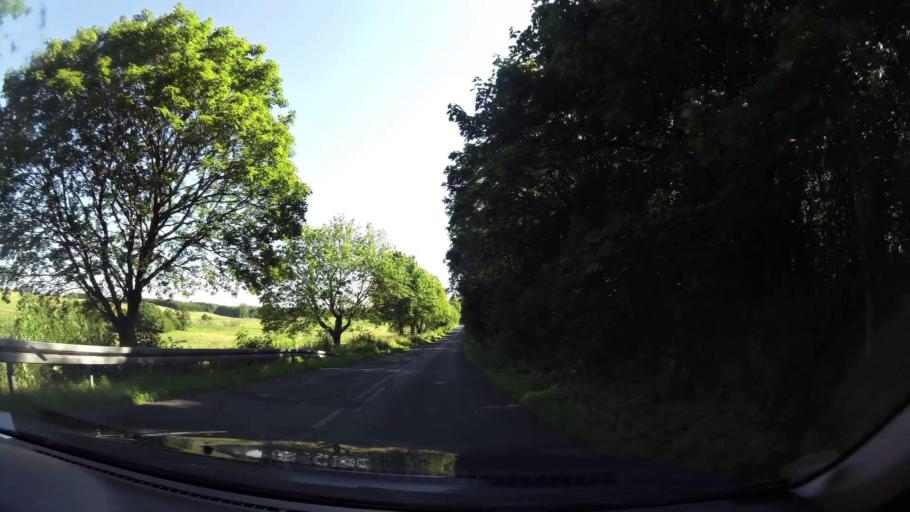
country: PL
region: West Pomeranian Voivodeship
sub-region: Powiat stargardzki
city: Dobrzany
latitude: 53.4156
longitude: 15.4188
